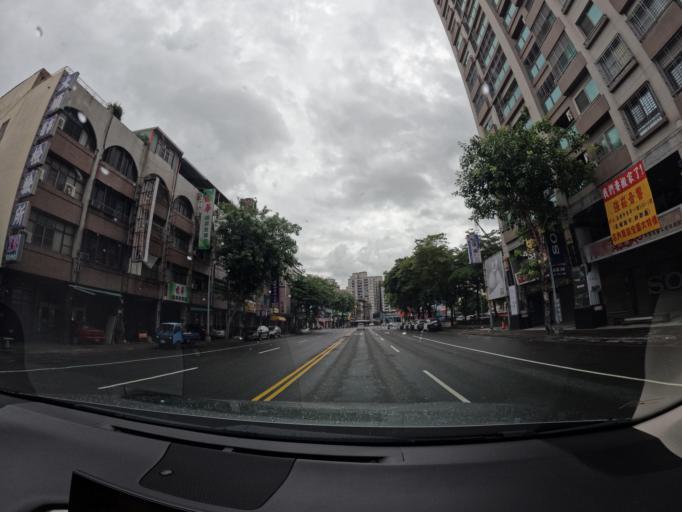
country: TW
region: Kaohsiung
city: Kaohsiung
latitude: 22.6329
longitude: 120.3272
